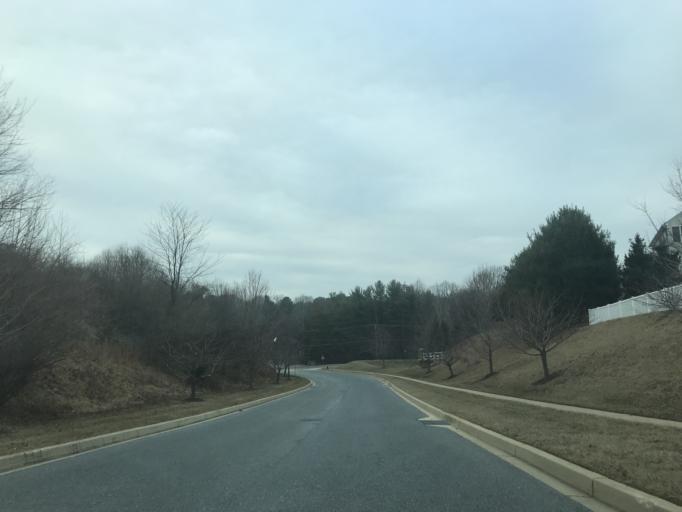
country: US
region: Maryland
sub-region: Carroll County
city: Eldersburg
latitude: 39.3752
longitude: -76.9279
